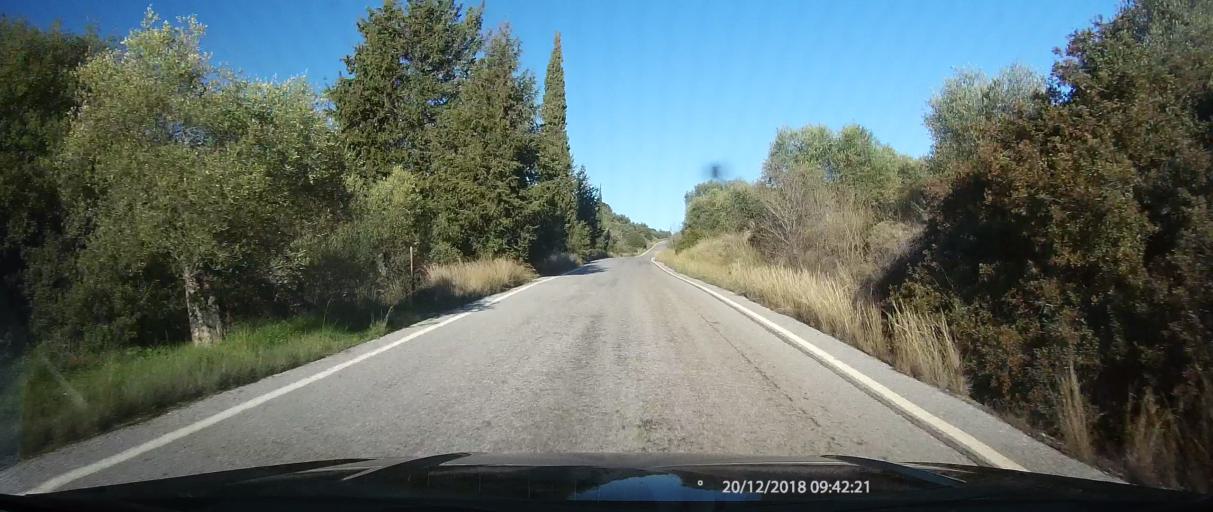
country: GR
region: Peloponnese
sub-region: Nomos Lakonias
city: Yerakion
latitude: 36.9587
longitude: 22.7556
